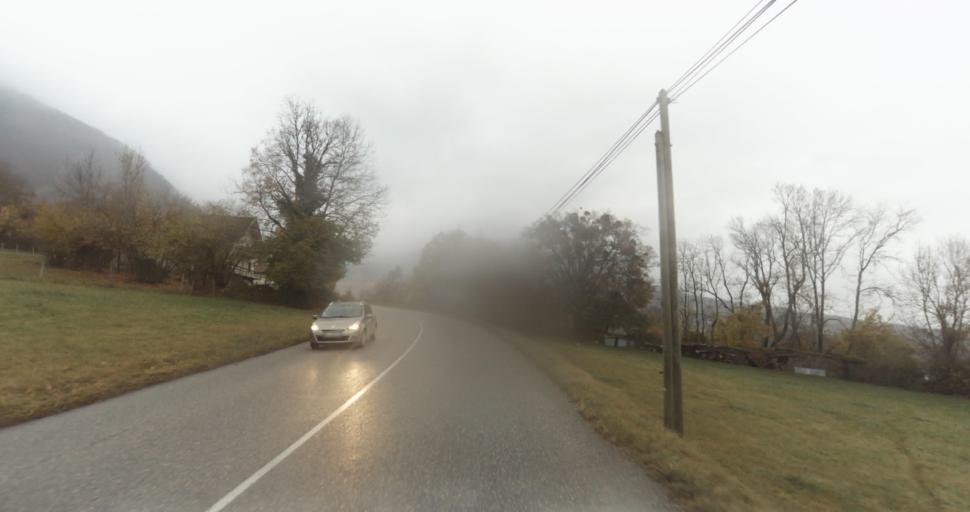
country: FR
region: Rhone-Alpes
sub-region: Departement de la Haute-Savoie
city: Gruffy
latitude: 45.7803
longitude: 6.0528
